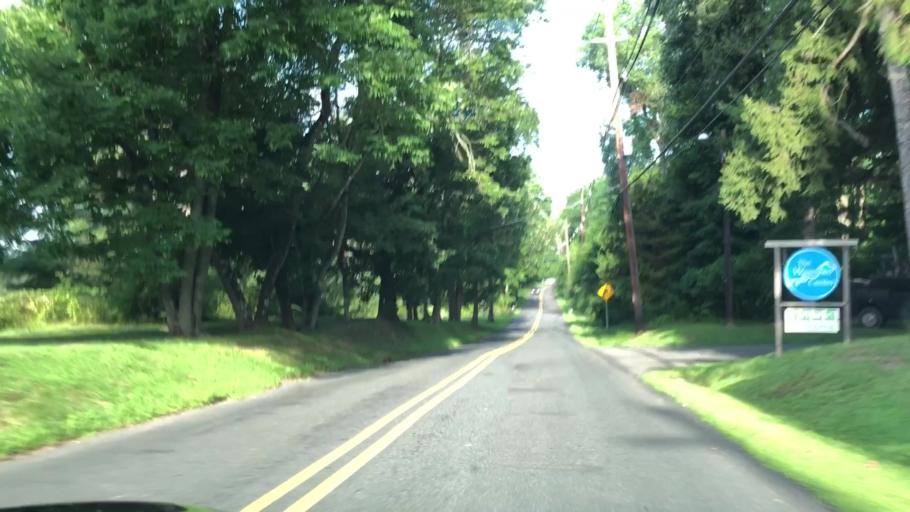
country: US
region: New Jersey
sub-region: Mercer County
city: Pennington
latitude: 40.3497
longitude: -74.7719
